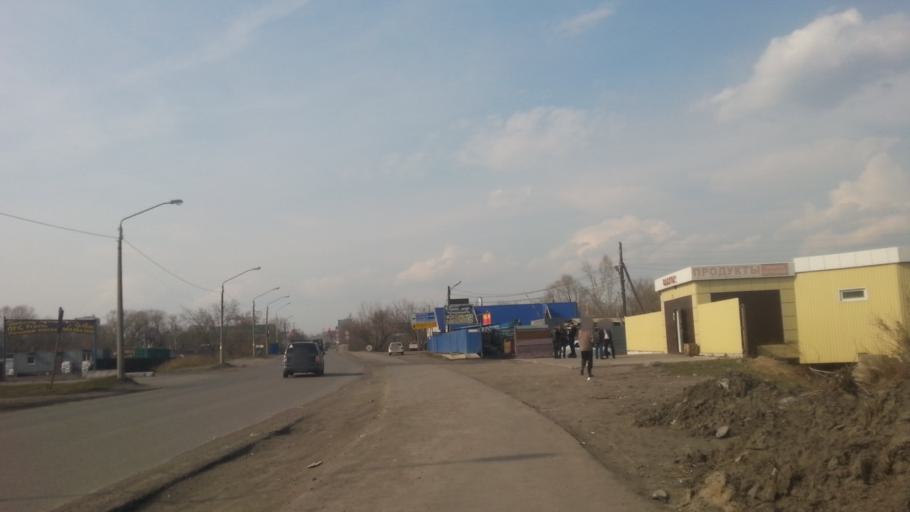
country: RU
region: Altai Krai
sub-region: Gorod Barnaulskiy
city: Barnaul
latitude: 53.3215
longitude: 83.7692
